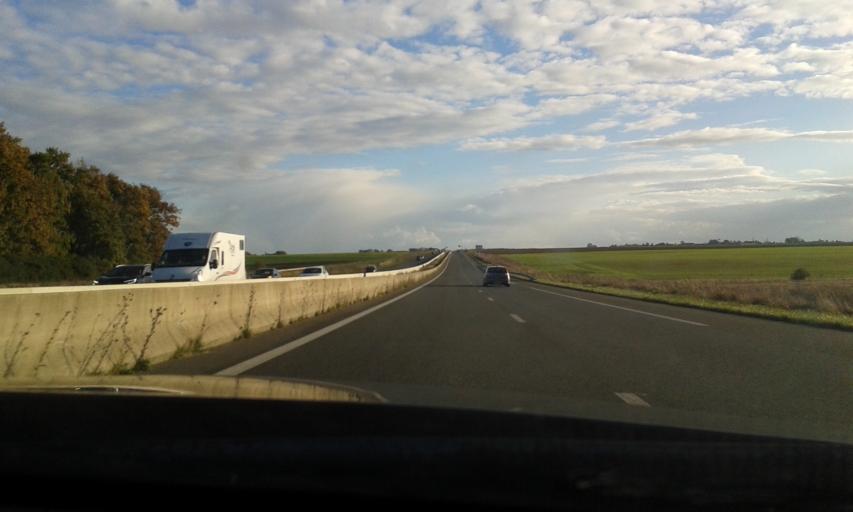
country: FR
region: Centre
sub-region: Departement d'Eure-et-Loir
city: Bailleau-l'Eveque
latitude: 48.5744
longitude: 1.4340
